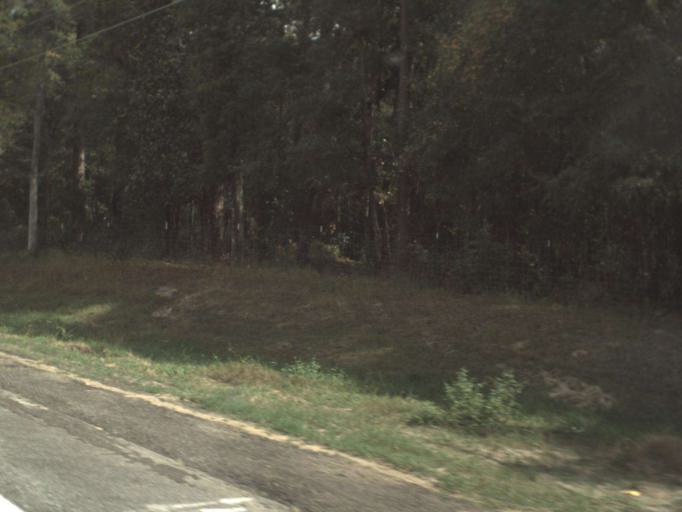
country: US
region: Florida
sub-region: Gadsden County
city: Havana
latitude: 30.5871
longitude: -84.4890
